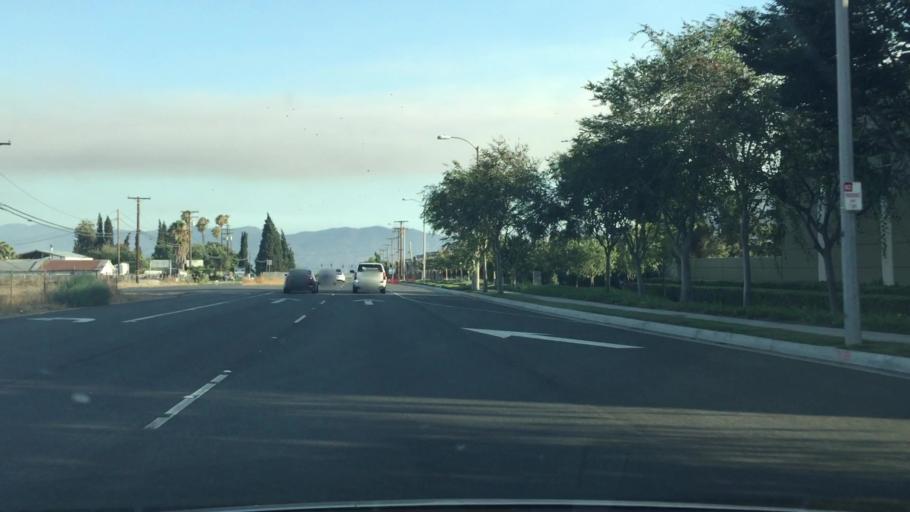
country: US
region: California
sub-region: San Bernardino County
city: Chino
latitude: 33.9944
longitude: -117.6509
